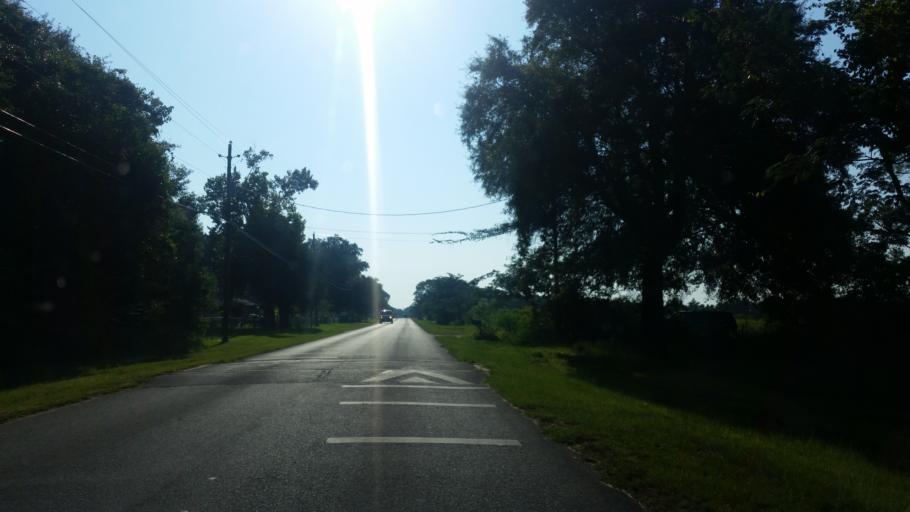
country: US
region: Florida
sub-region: Escambia County
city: Bellview
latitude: 30.4761
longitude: -87.3199
